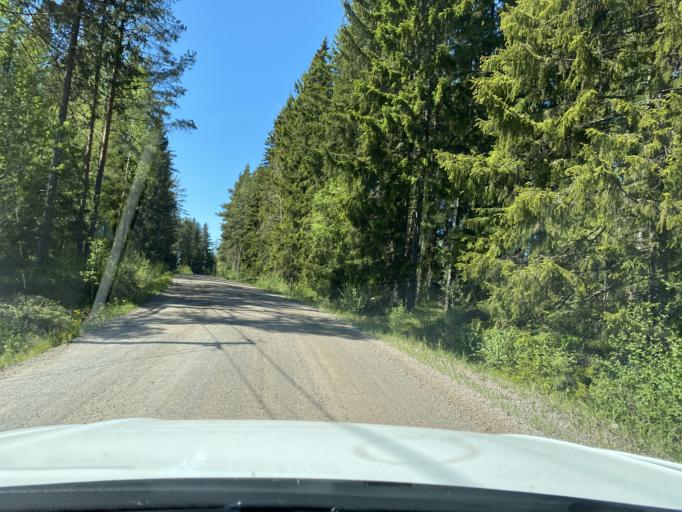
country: FI
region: Satakunta
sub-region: Rauma
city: Kiukainen
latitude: 61.1343
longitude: 21.9845
